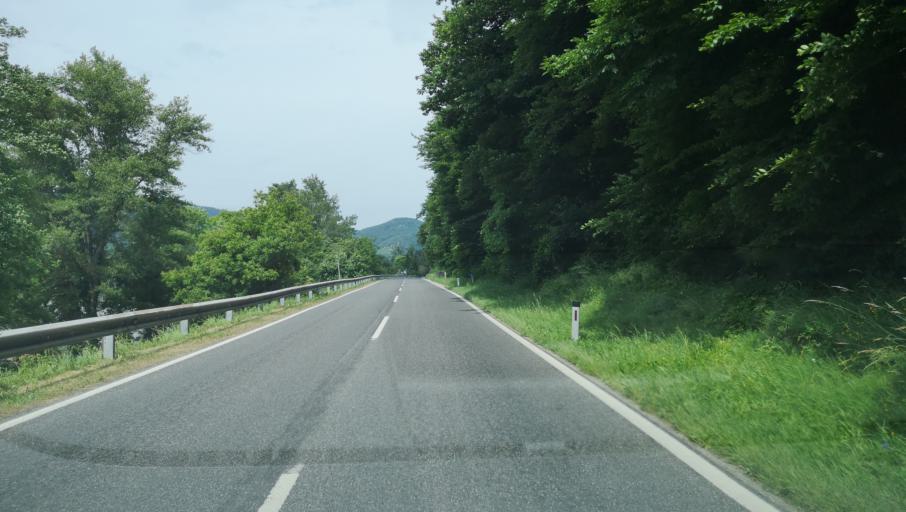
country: AT
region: Lower Austria
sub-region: Politischer Bezirk Krems
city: Durnstein
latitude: 48.3892
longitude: 15.4711
